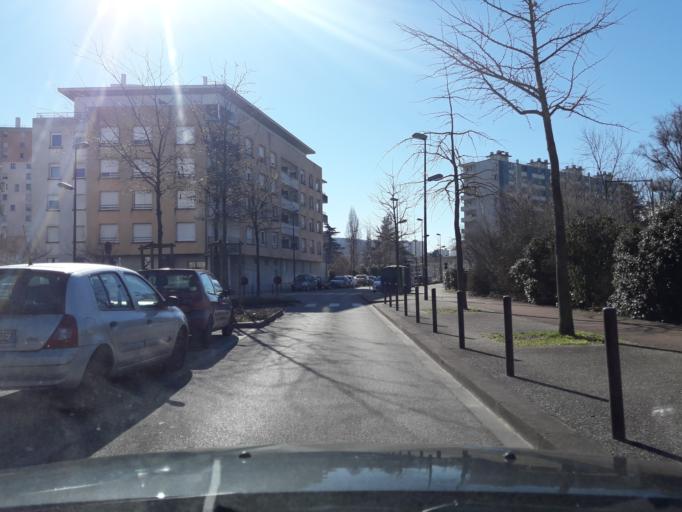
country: FR
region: Rhone-Alpes
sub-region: Departement de l'Isere
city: Echirolles
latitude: 45.1451
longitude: 5.7192
